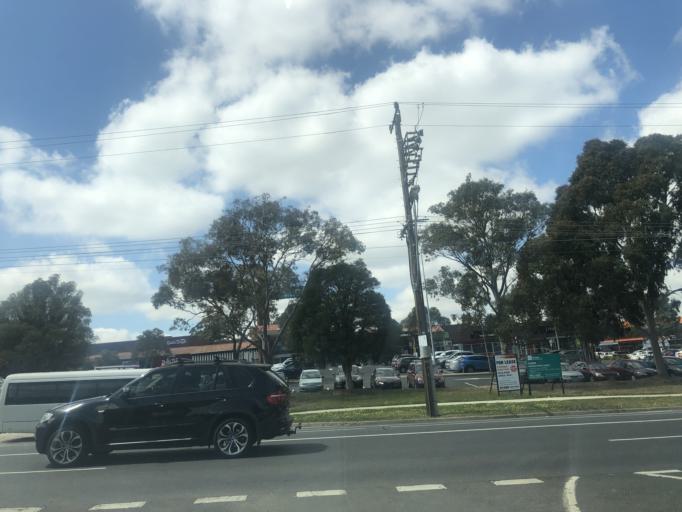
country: AU
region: Victoria
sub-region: Monash
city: Mulgrave
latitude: -37.9080
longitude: 145.1866
